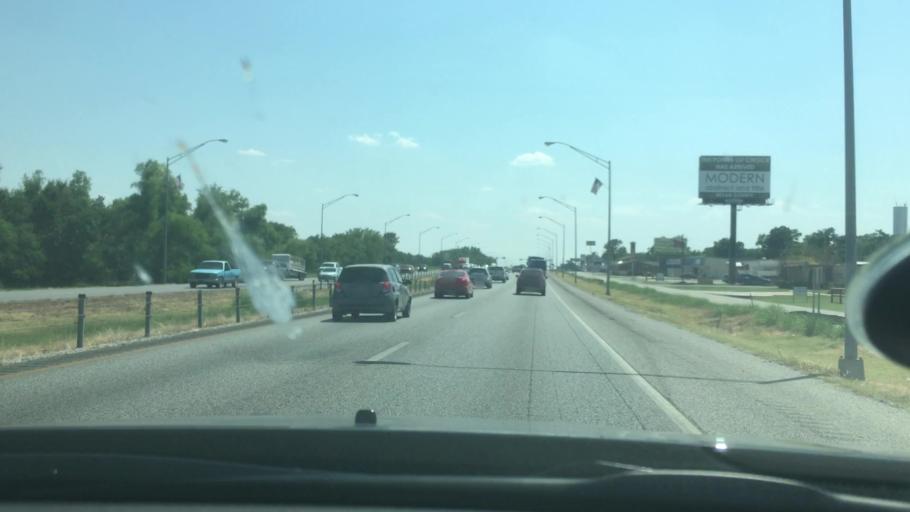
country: US
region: Oklahoma
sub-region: Bryan County
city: Calera
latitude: 33.9367
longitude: -96.4241
